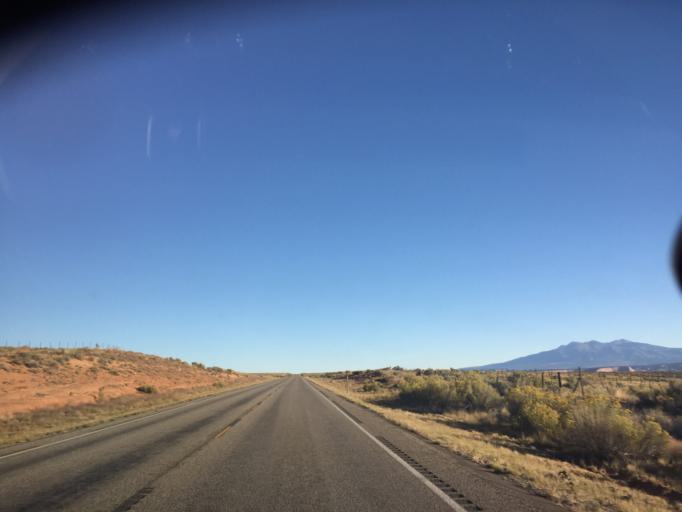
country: US
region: Utah
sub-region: San Juan County
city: Monticello
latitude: 38.1184
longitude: -109.3661
